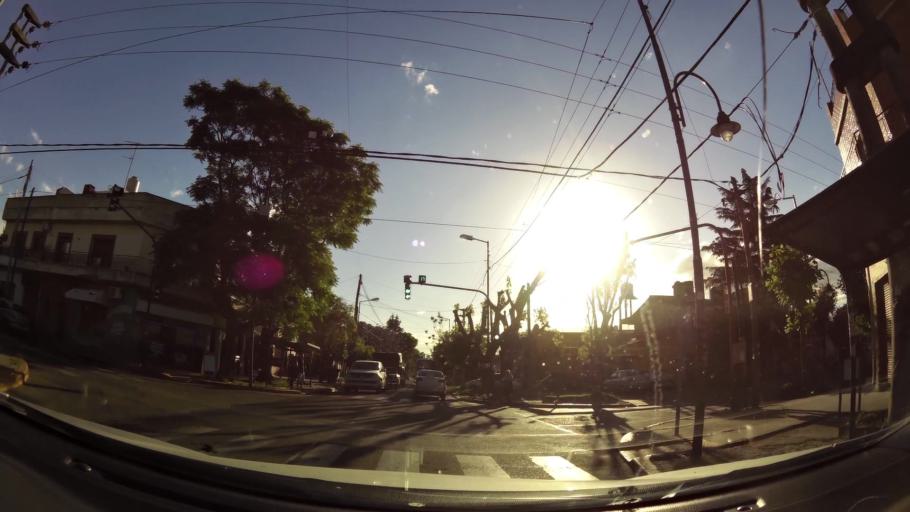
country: AR
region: Buenos Aires
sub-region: Partido de Tigre
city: Tigre
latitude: -34.4618
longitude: -58.5621
